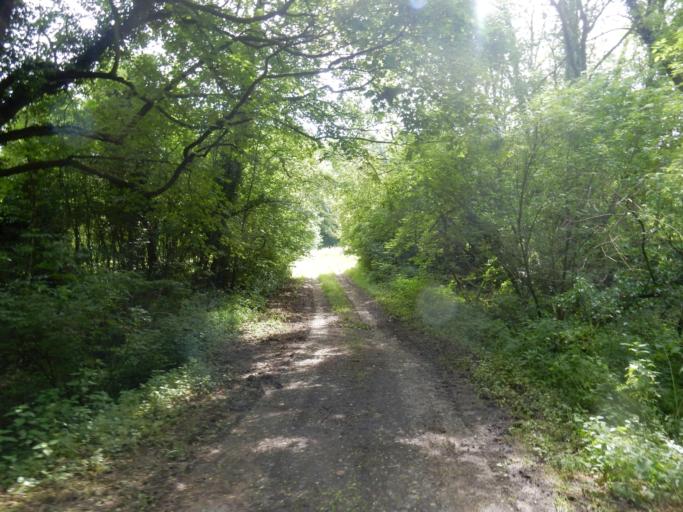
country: FR
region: Lorraine
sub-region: Departement de Meurthe-et-Moselle
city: Pagny-sur-Moselle
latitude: 48.9719
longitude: 5.9782
